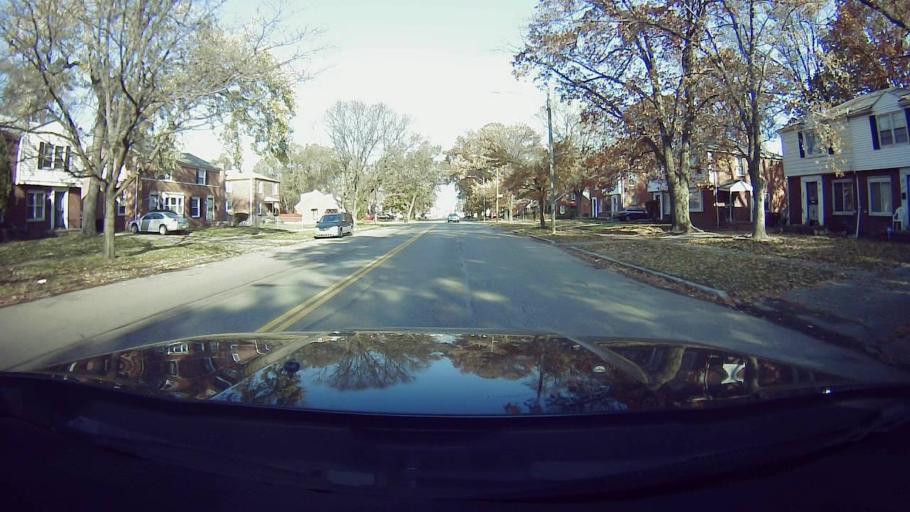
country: US
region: Michigan
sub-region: Oakland County
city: Oak Park
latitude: 42.4070
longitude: -83.1696
